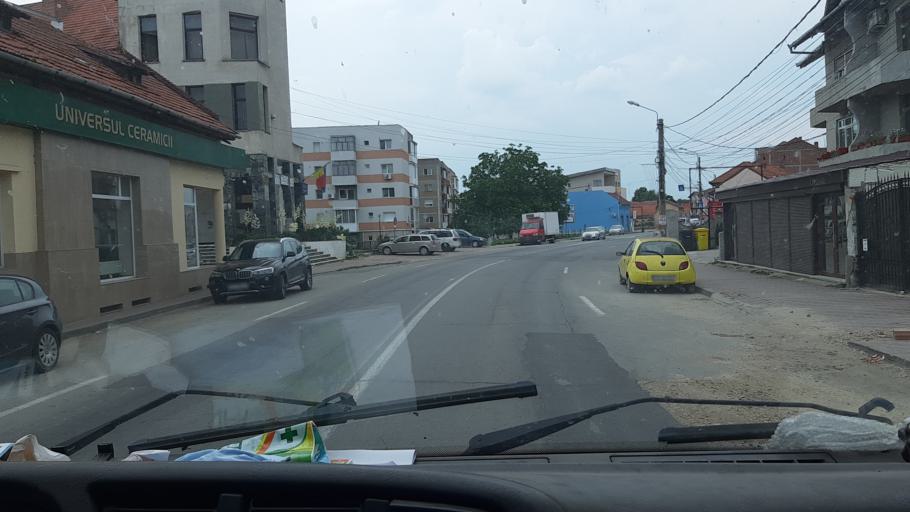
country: RO
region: Timis
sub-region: Municipiul Lugoj
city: Lugoj
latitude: 45.6920
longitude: 21.9023
